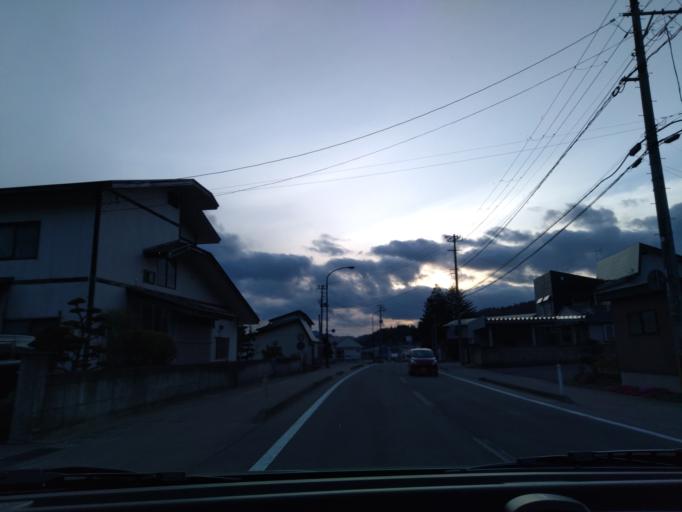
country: JP
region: Akita
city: Kakunodatemachi
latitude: 39.5938
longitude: 140.5795
